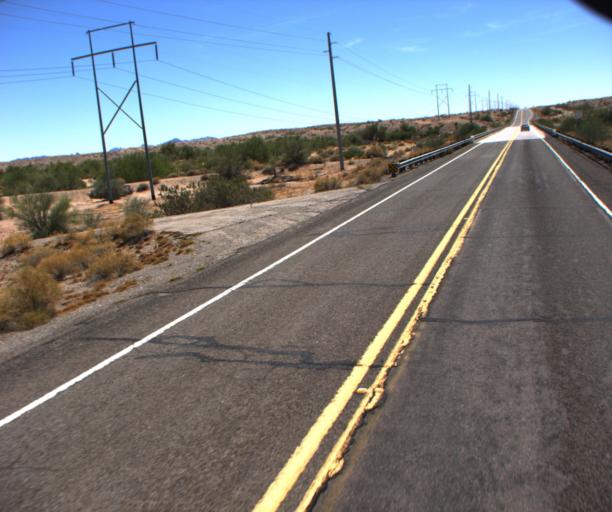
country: US
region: Arizona
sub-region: La Paz County
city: Parker
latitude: 33.9920
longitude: -114.2169
